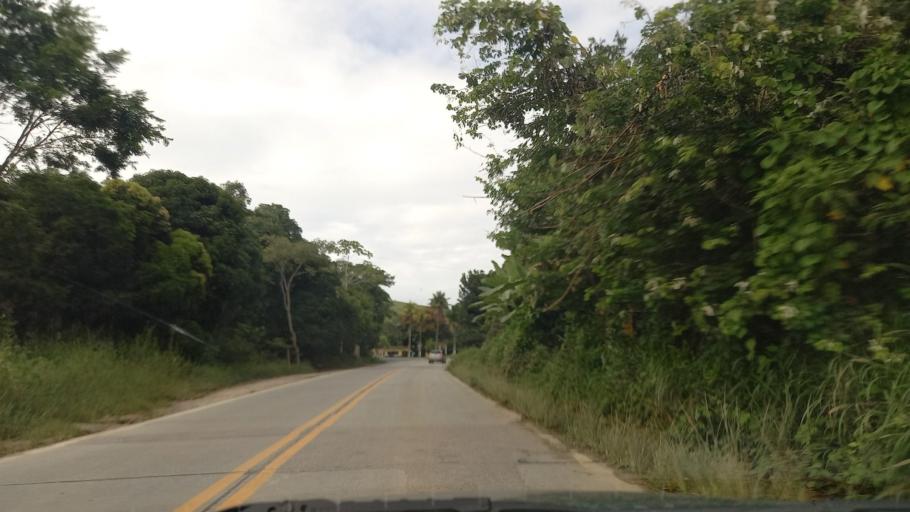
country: BR
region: Pernambuco
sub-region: Catende
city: Catende
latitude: -8.6926
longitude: -35.7240
